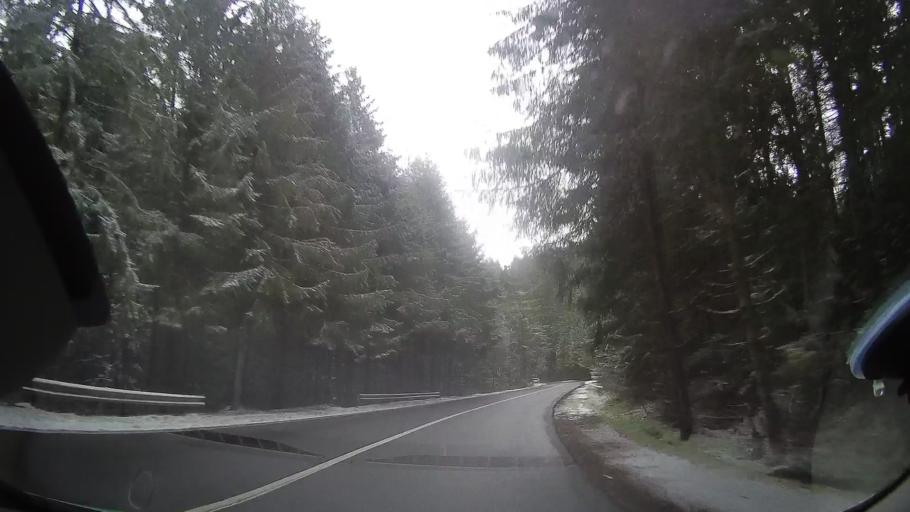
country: RO
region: Cluj
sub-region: Comuna Calatele
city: Calatele
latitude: 46.7315
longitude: 23.0371
